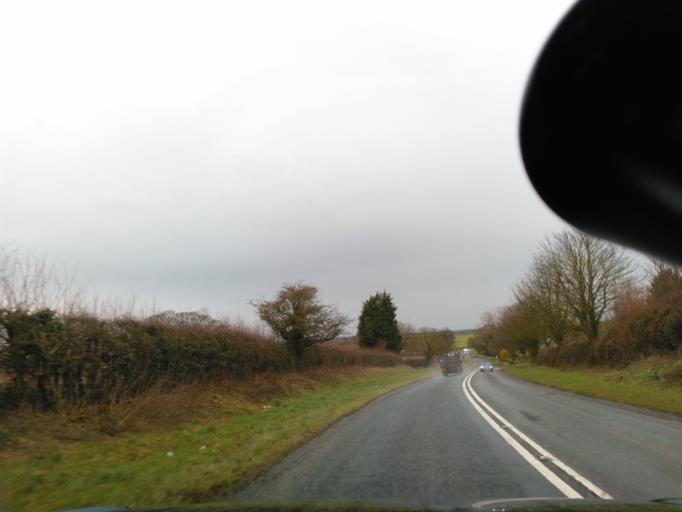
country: GB
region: England
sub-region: North Yorkshire
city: Northallerton
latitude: 54.3045
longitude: -1.3982
